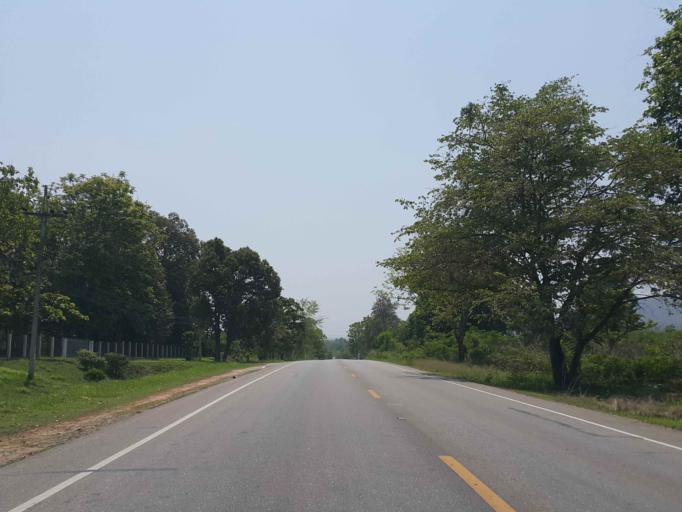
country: TH
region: Chiang Mai
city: Mae Taeng
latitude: 19.1102
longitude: 99.0277
